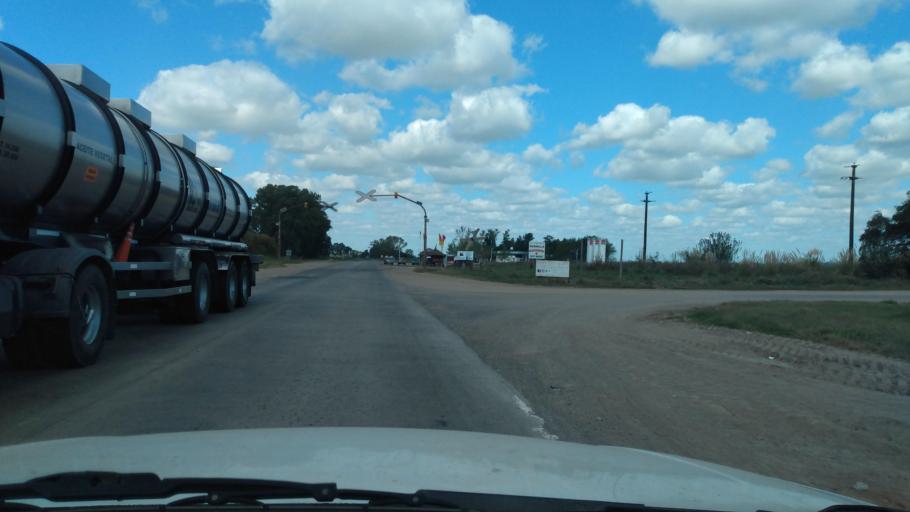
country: AR
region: Buenos Aires
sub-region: Partido de Navarro
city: Navarro
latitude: -34.9958
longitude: -59.3145
